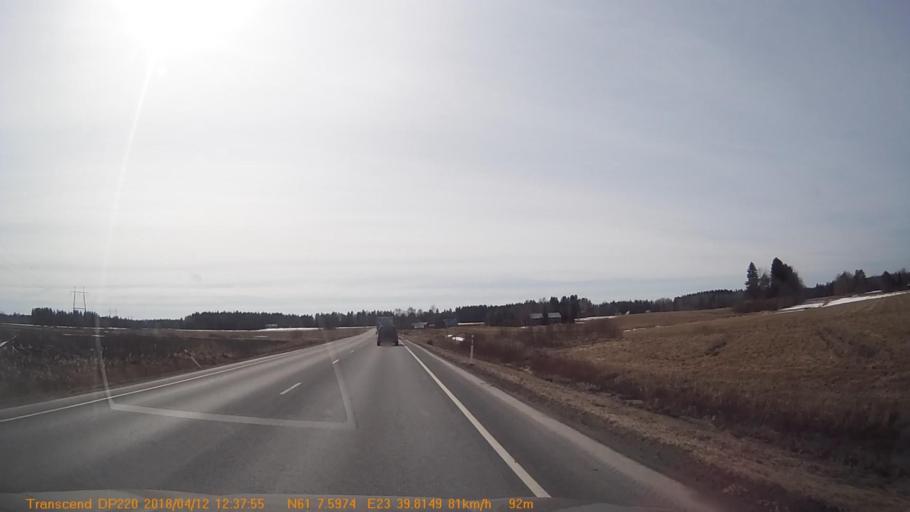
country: FI
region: Pirkanmaa
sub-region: Etelae-Pirkanmaa
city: Kylmaekoski
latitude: 61.1267
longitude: 23.6637
